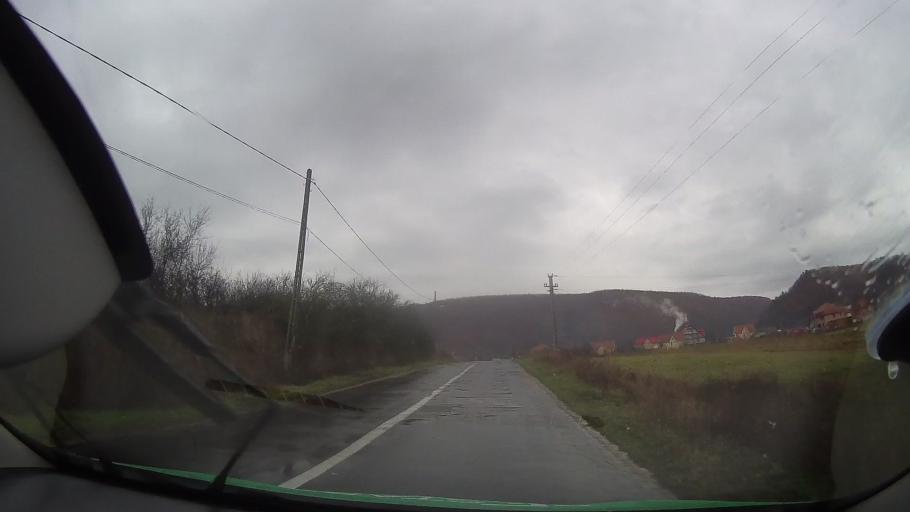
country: RO
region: Bihor
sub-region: Comuna Soimi
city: Soimi
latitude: 46.6833
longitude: 22.1143
